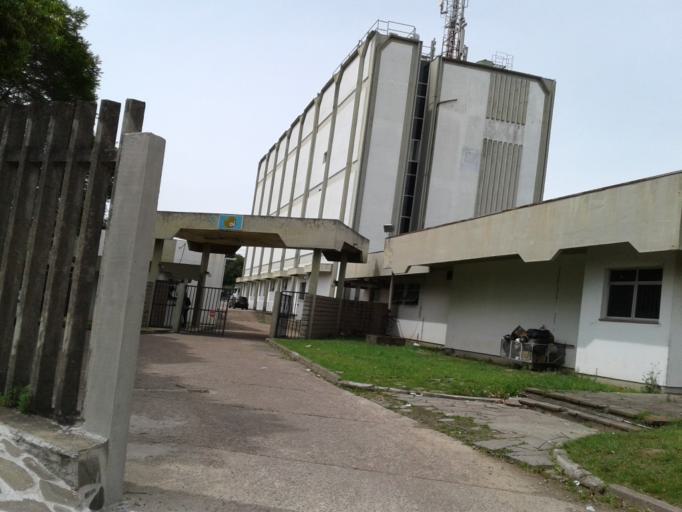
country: BR
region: Rio Grande do Sul
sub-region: Porto Alegre
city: Porto Alegre
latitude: -30.1372
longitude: -51.2214
